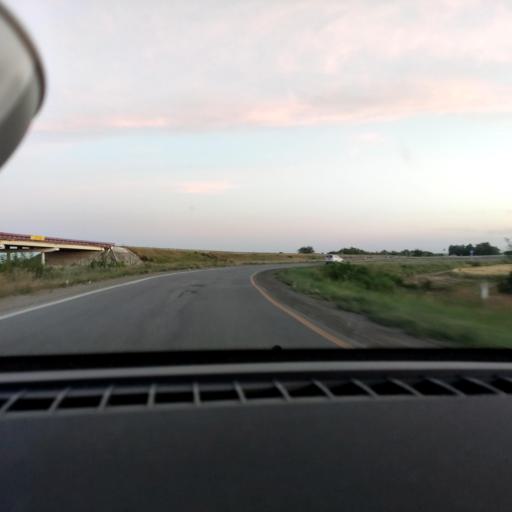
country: RU
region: Samara
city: Kinel'
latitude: 53.2642
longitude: 50.5430
